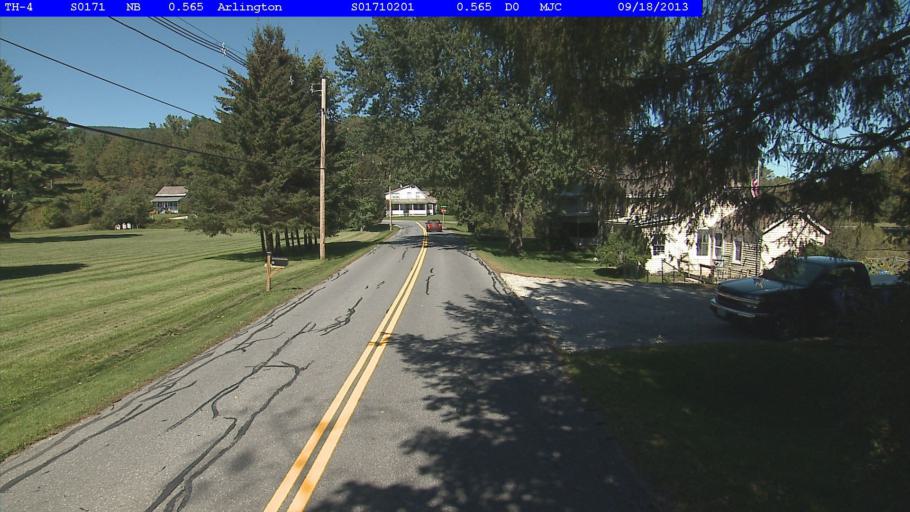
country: US
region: Vermont
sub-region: Bennington County
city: Arlington
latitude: 43.0613
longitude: -73.1471
